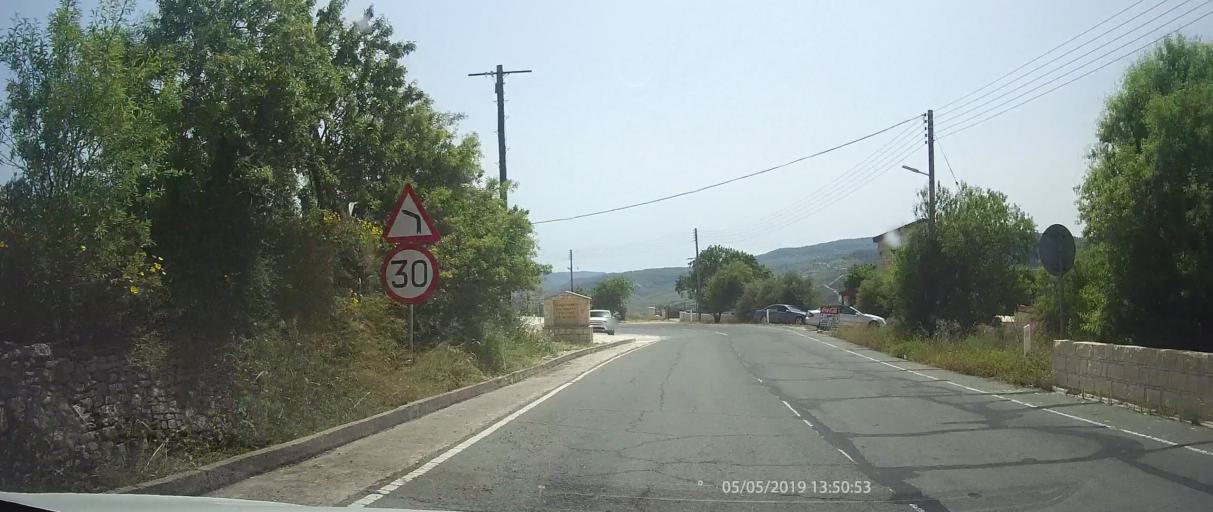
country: CY
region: Limassol
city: Pachna
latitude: 34.8390
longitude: 32.7357
